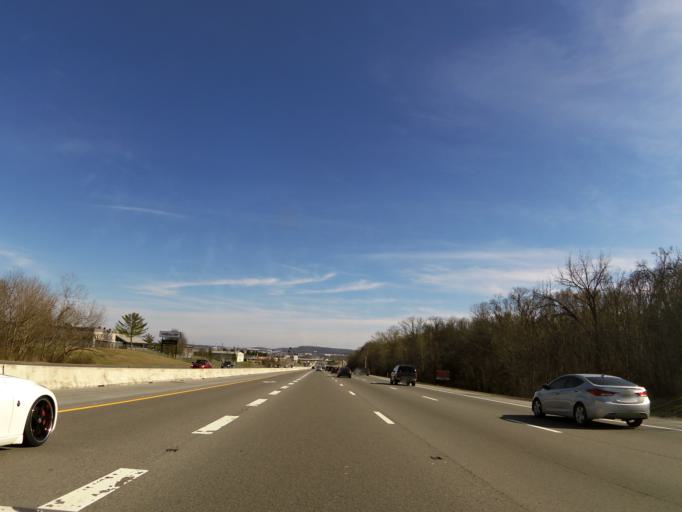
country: US
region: Tennessee
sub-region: Rutherford County
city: La Vergne
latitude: 36.0204
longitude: -86.6274
